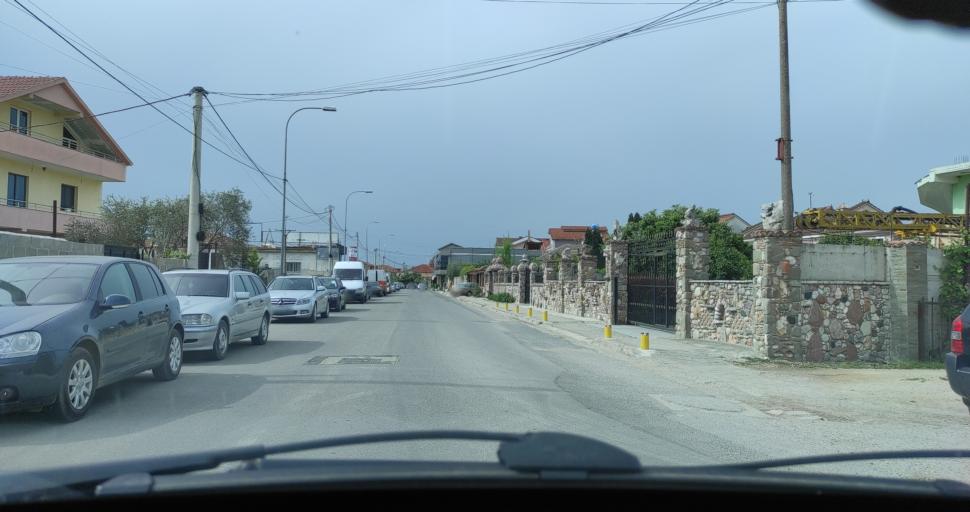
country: AL
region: Durres
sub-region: Rrethi i Krujes
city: Fushe-Kruje
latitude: 41.4712
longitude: 19.7200
